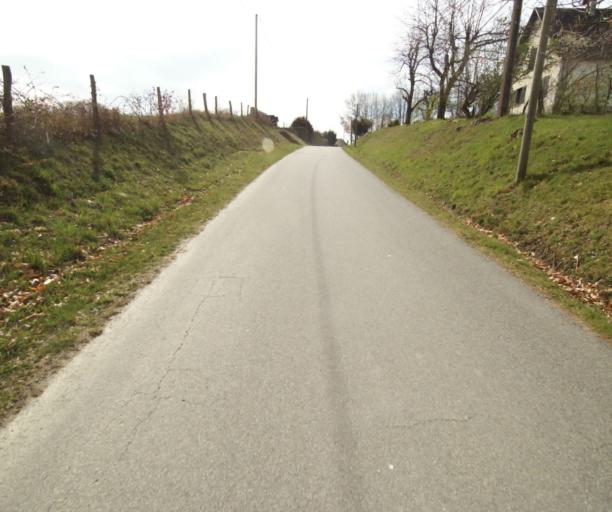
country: FR
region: Limousin
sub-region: Departement de la Correze
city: Correze
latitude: 45.3688
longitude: 1.8840
